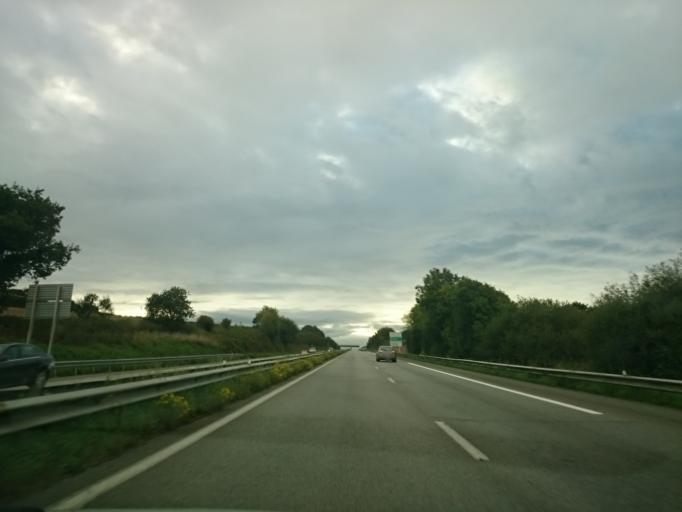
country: FR
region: Brittany
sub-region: Departement du Finistere
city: Chateaulin
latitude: 48.2217
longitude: -4.0664
